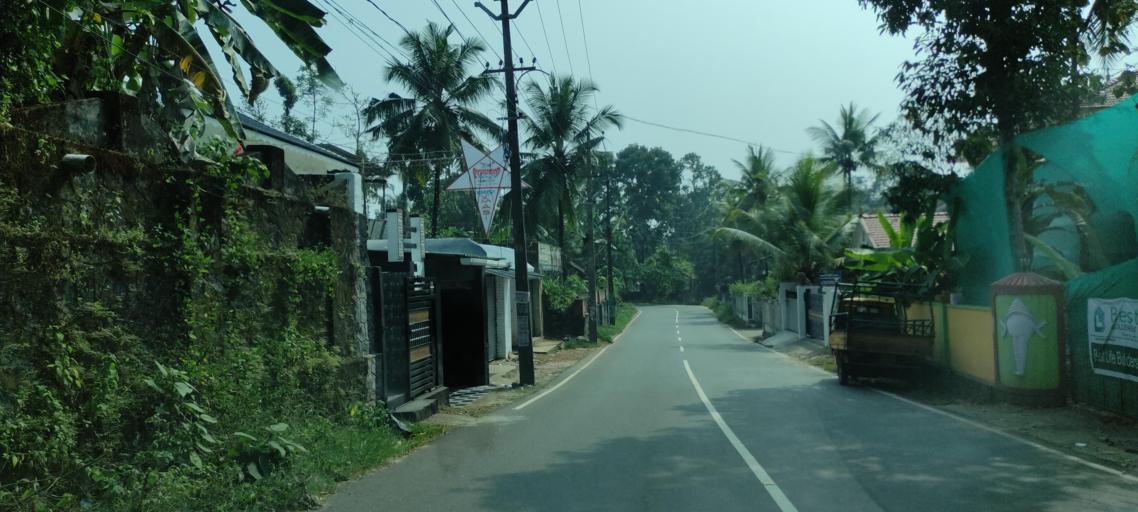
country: IN
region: Kerala
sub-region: Alappuzha
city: Chengannur
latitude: 9.2436
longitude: 76.6759
